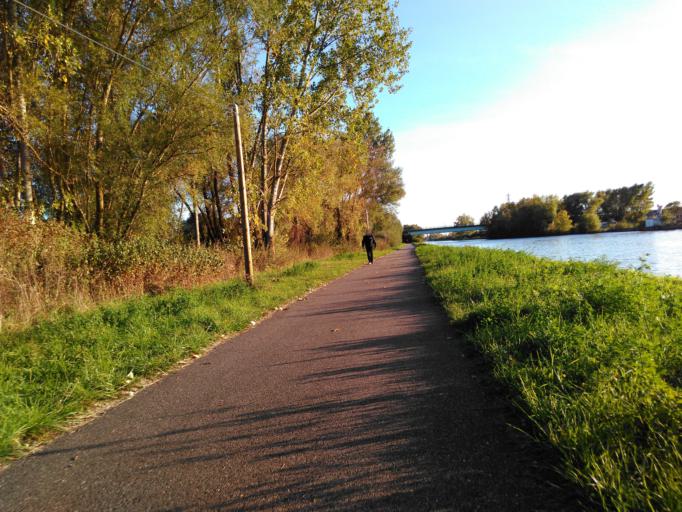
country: FR
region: Lorraine
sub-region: Departement de la Moselle
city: Talange
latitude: 49.2213
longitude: 6.1829
